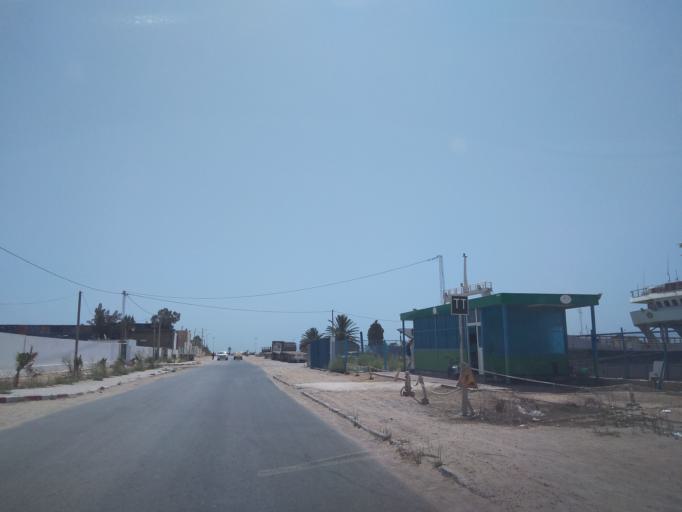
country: TN
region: Safaqis
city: Al Qarmadah
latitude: 34.7294
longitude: 10.7794
